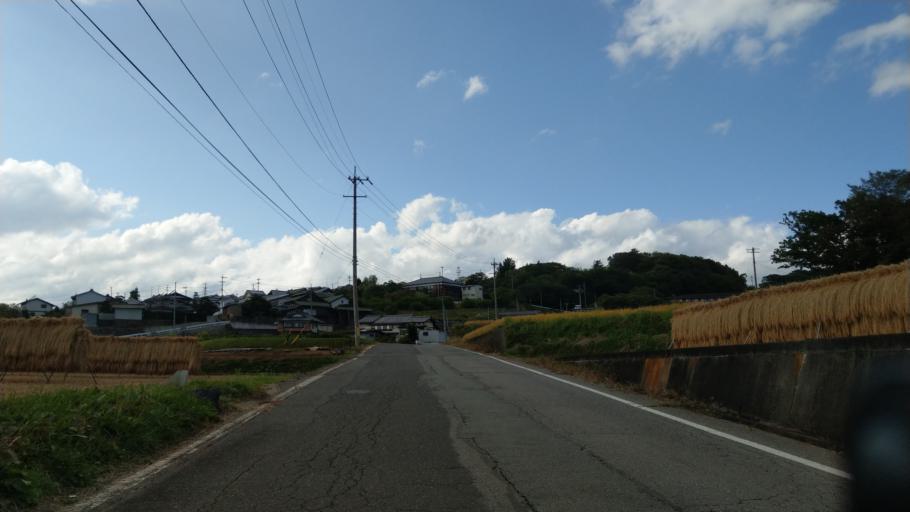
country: JP
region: Nagano
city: Komoro
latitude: 36.3479
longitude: 138.4136
